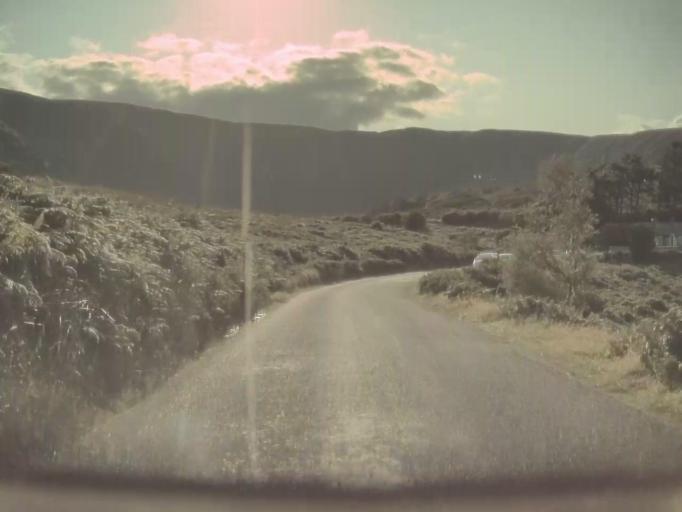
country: IE
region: Leinster
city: Ballyboden
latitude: 53.1898
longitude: -6.3000
